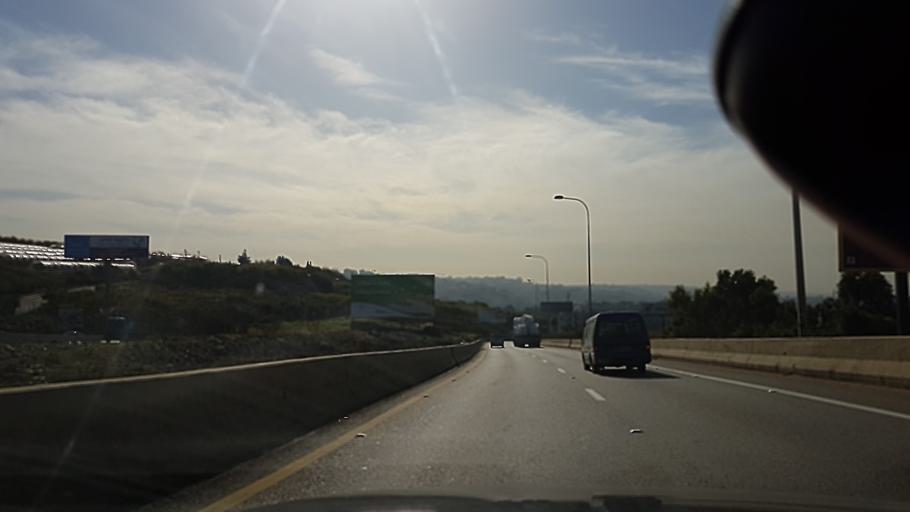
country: LB
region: Liban-Sud
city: Sidon
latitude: 33.6008
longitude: 35.3907
